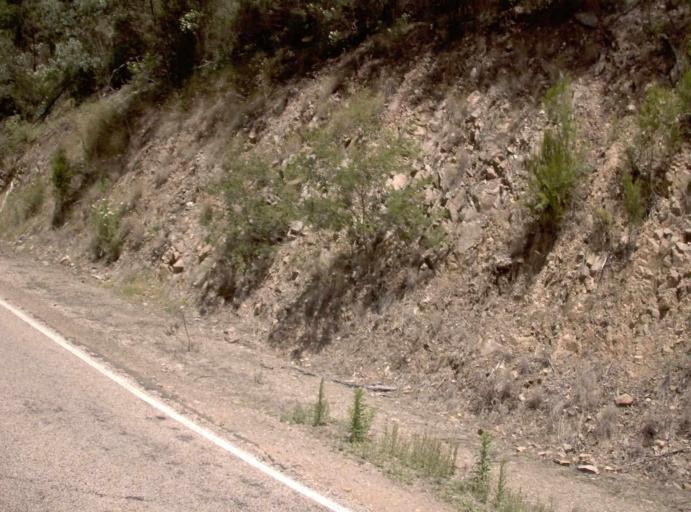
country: AU
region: Victoria
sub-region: East Gippsland
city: Lakes Entrance
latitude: -37.5304
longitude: 147.8534
